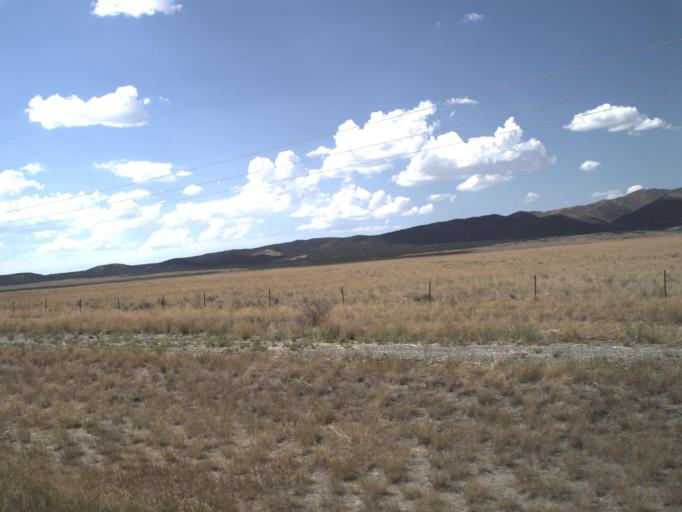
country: US
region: Idaho
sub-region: Power County
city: American Falls
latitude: 41.9678
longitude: -113.0912
